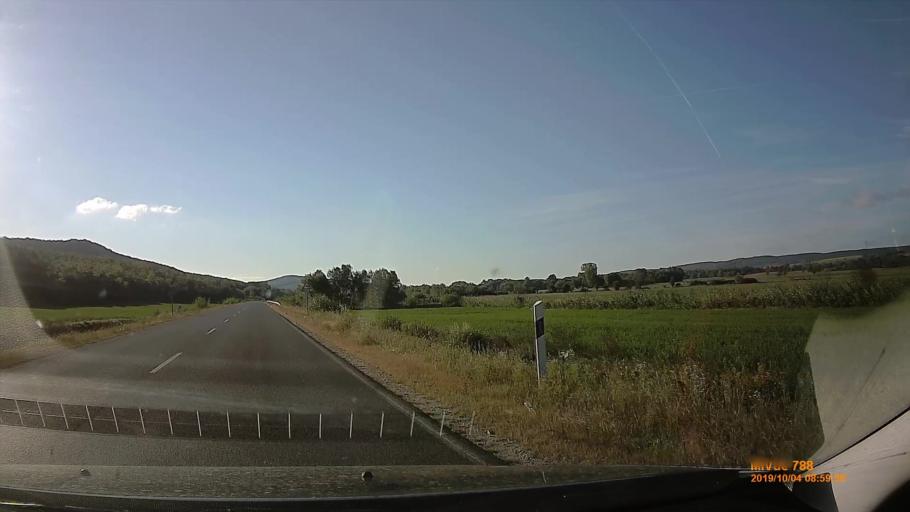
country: HU
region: Somogy
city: Balatonlelle
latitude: 46.7545
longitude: 17.7673
